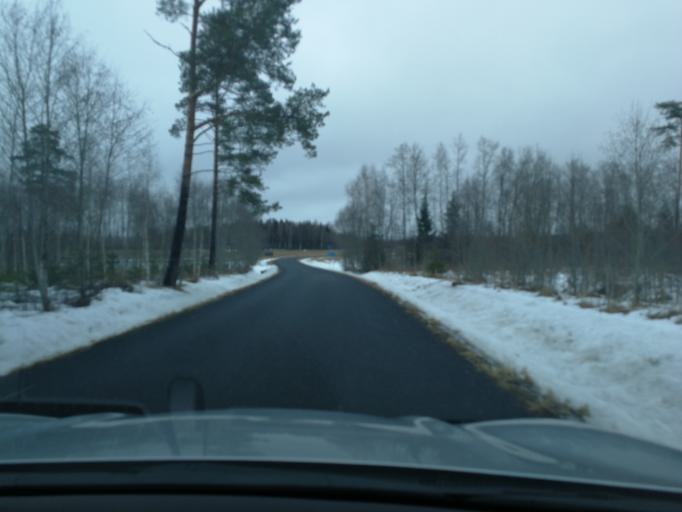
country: EE
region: Harju
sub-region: Rae vald
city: Vaida
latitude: 59.2328
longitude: 25.0193
